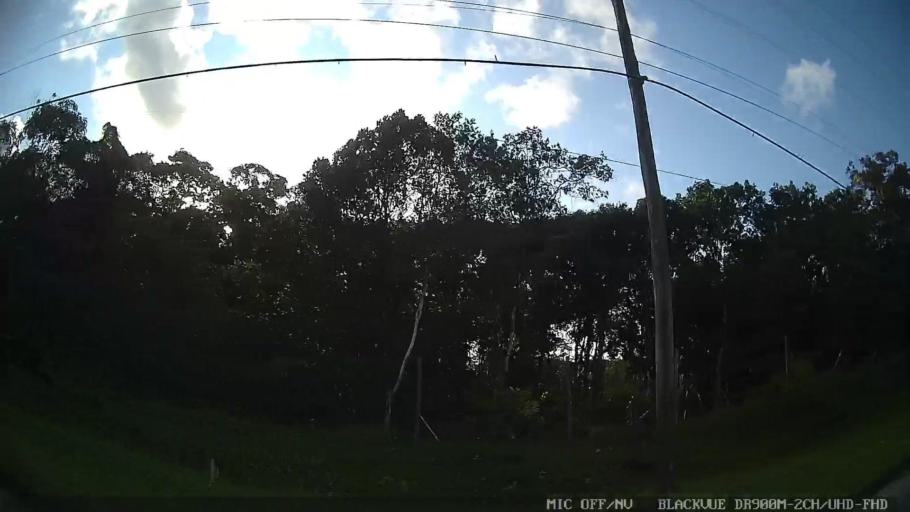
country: BR
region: Sao Paulo
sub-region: Itanhaem
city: Itanhaem
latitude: -24.1524
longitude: -46.8223
